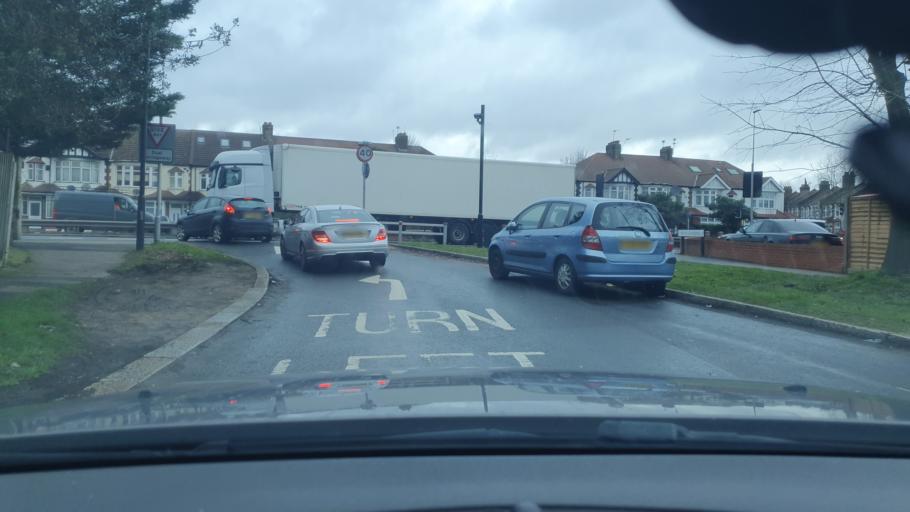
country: GB
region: England
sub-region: Greater London
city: Wood Green
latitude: 51.6139
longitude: -0.1022
